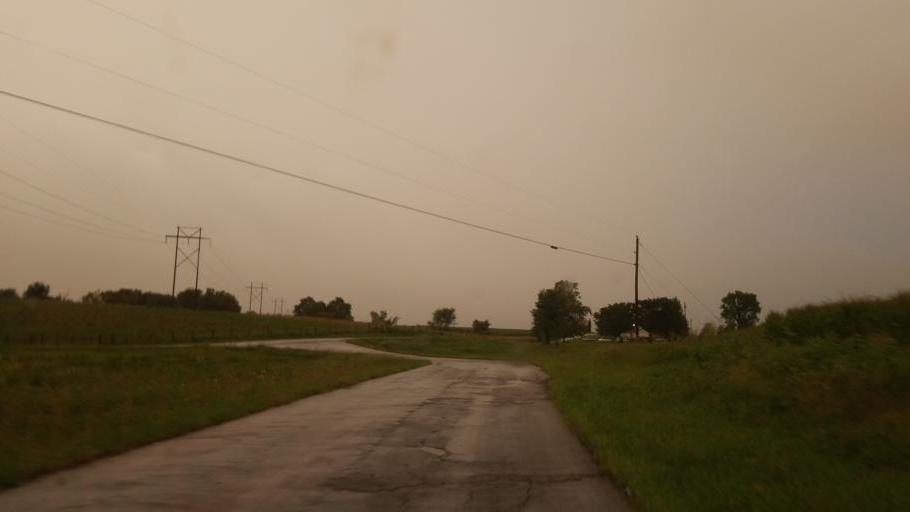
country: US
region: Kentucky
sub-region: Fleming County
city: Flemingsburg
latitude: 38.4688
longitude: -83.6374
